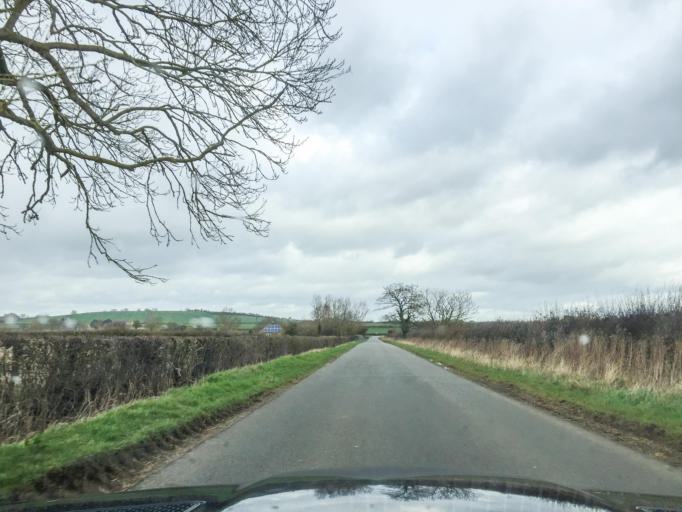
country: GB
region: England
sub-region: Warwickshire
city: Shipston on Stour
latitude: 52.1004
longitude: -1.5729
